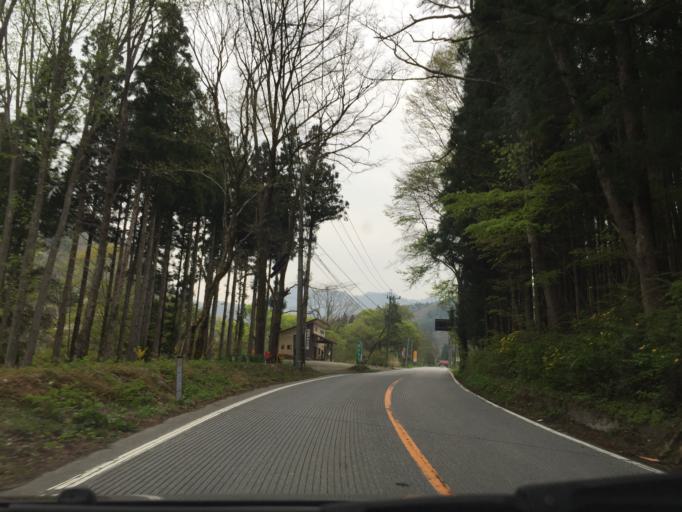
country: JP
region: Tochigi
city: Nikko
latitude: 36.9731
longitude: 139.6885
